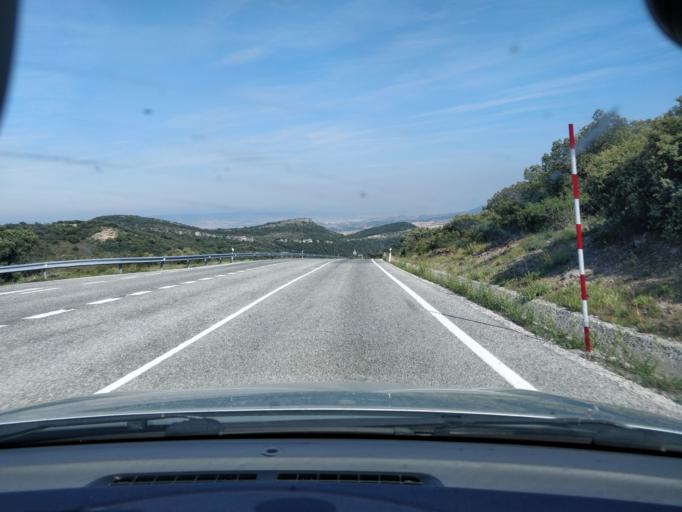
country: ES
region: Castille and Leon
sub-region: Provincia de Burgos
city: Medina de Pomar
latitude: 42.9196
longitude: -3.6189
